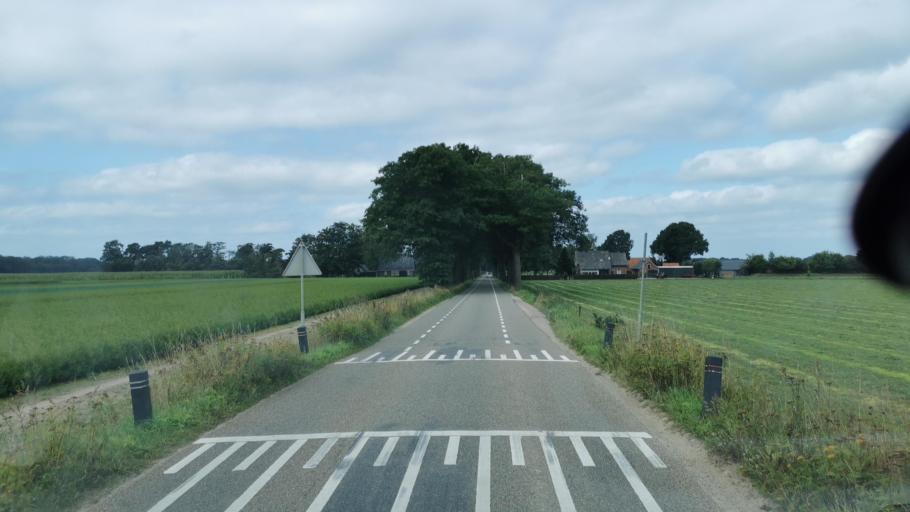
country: NL
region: Overijssel
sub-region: Gemeente Oldenzaal
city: Oldenzaal
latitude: 52.3185
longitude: 6.8842
